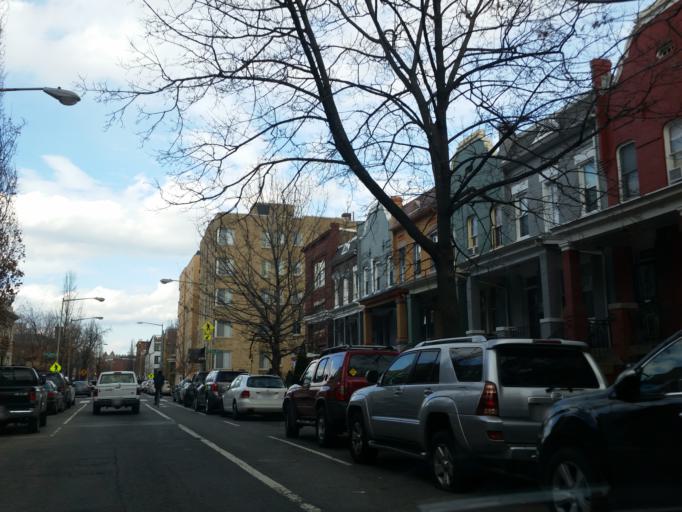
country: US
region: Washington, D.C.
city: Washington, D.C.
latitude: 38.9242
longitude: -77.0353
